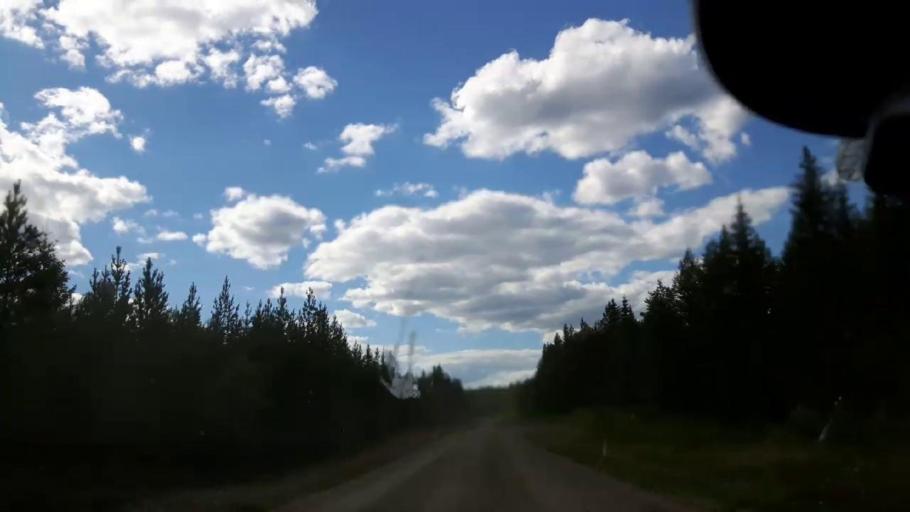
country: SE
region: Vaesternorrland
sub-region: Ange Kommun
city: Ange
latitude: 62.7681
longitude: 15.7723
